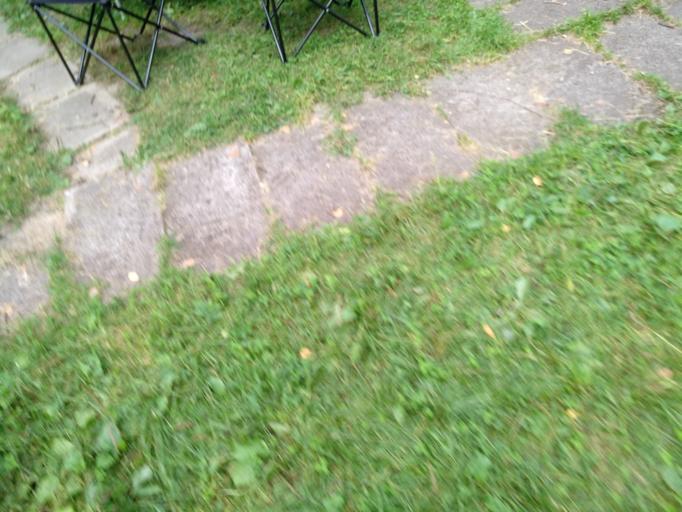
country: RU
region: Leningrad
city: Sapernoye
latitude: 60.6815
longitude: 29.9041
